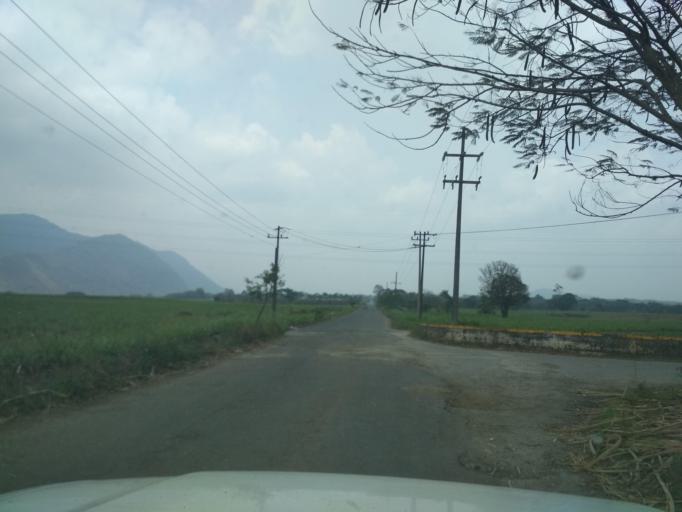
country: MX
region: Veracruz
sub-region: Cordoba
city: San Jose de Tapia
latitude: 18.8362
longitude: -96.9774
